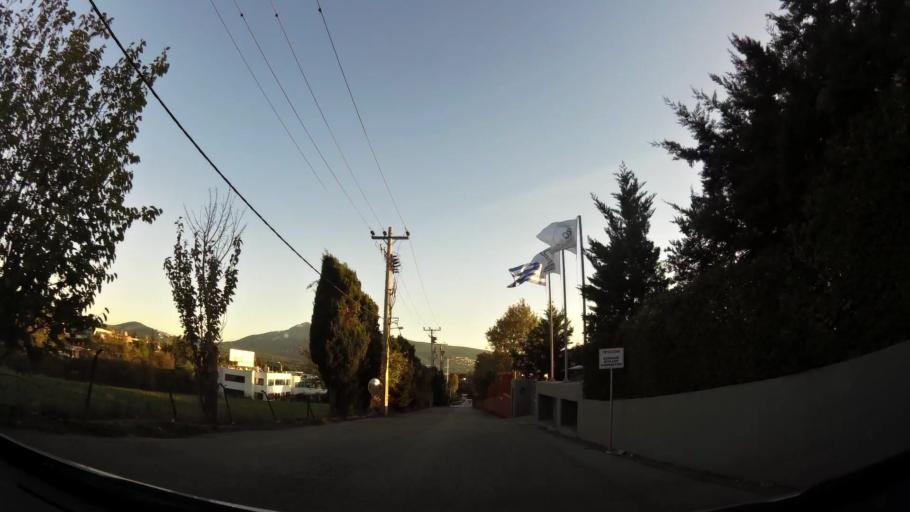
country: GR
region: Attica
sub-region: Nomarchia Anatolikis Attikis
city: Kryoneri
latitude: 38.1427
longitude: 23.8423
